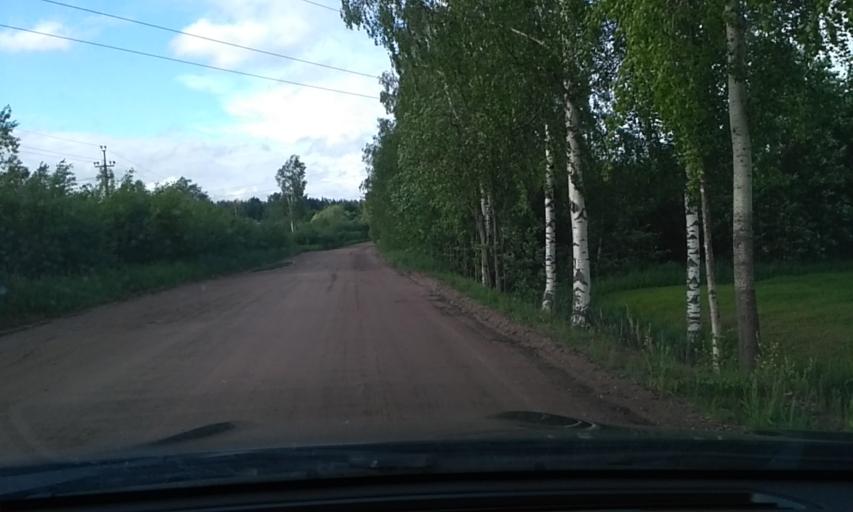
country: RU
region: Leningrad
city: Otradnoye
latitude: 59.8049
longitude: 30.8056
